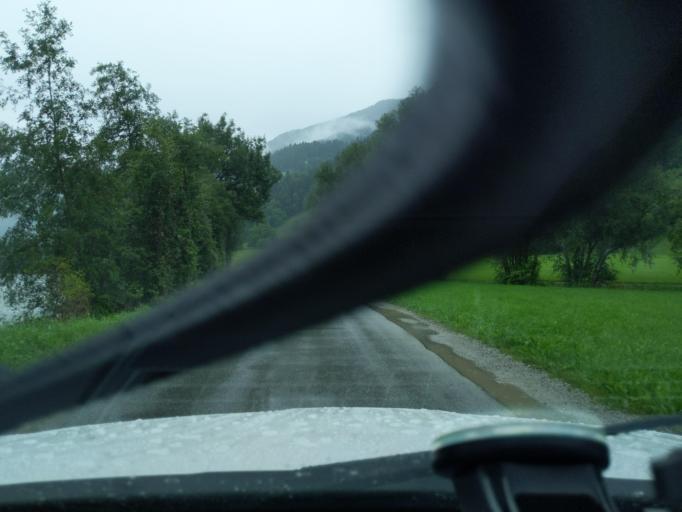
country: AT
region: Tyrol
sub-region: Politischer Bezirk Schwaz
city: Hart im Zillertal
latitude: 47.3548
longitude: 11.8664
